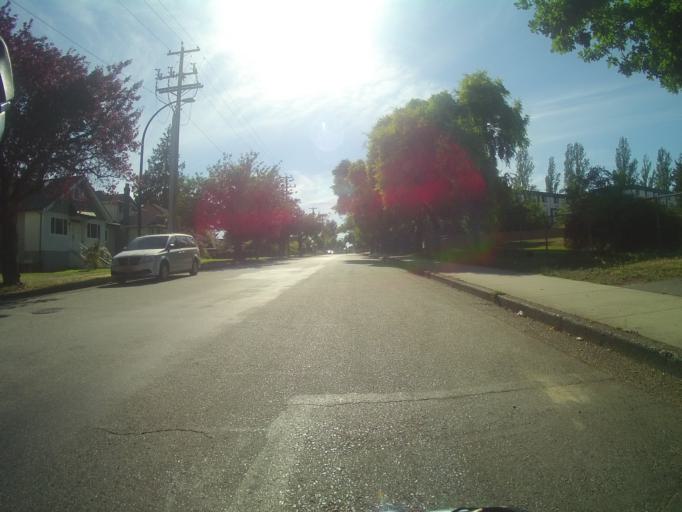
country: CA
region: British Columbia
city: Vancouver
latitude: 49.2170
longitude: -123.1223
